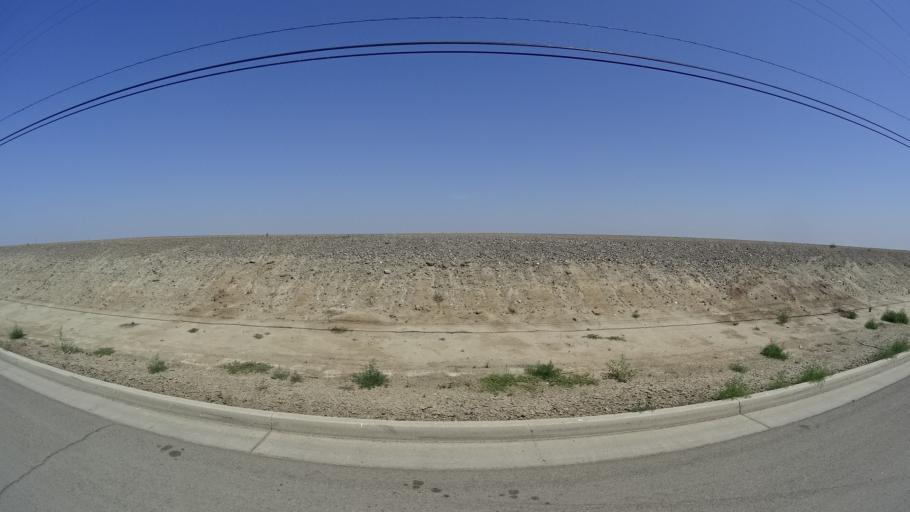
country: US
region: California
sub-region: Kings County
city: Home Garden
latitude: 36.2839
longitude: -119.6496
